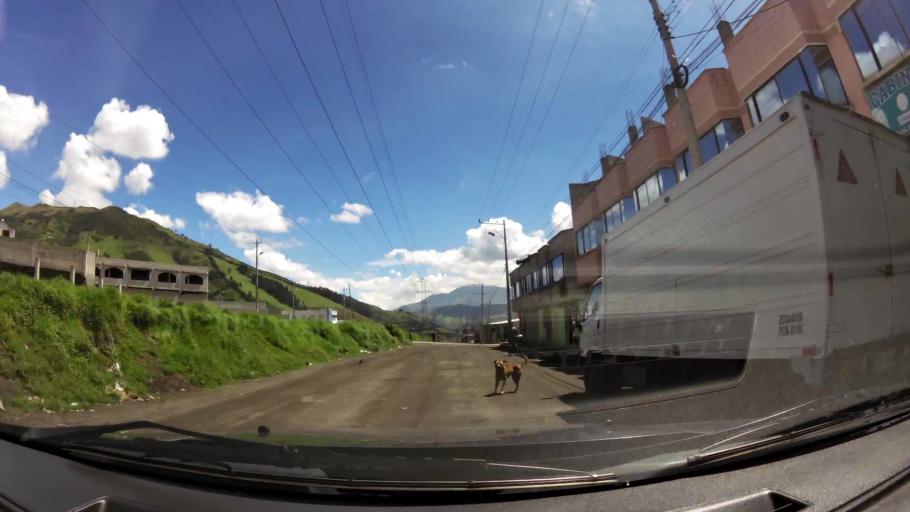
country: EC
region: Pichincha
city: Quito
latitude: -0.3274
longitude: -78.5683
